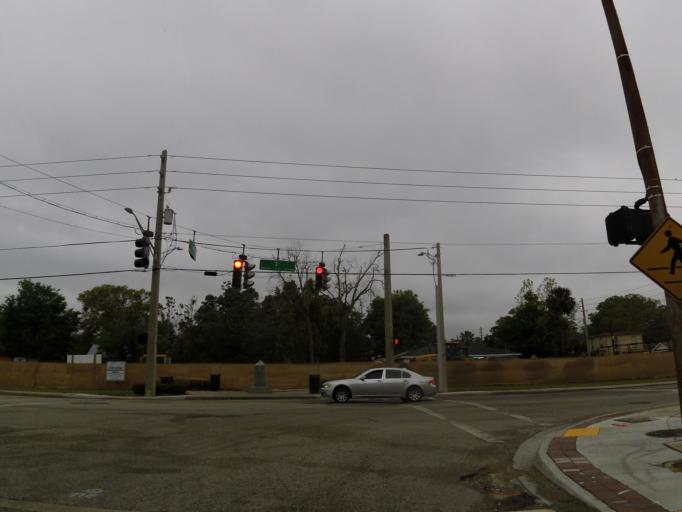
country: US
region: Florida
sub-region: Duval County
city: Jacksonville
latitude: 30.3363
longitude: -81.6426
